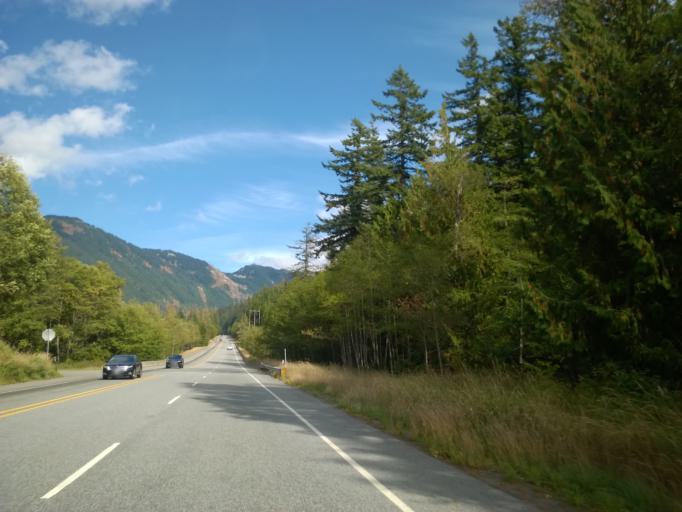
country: US
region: Washington
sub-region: Chelan County
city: Leavenworth
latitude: 47.7116
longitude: -121.1543
